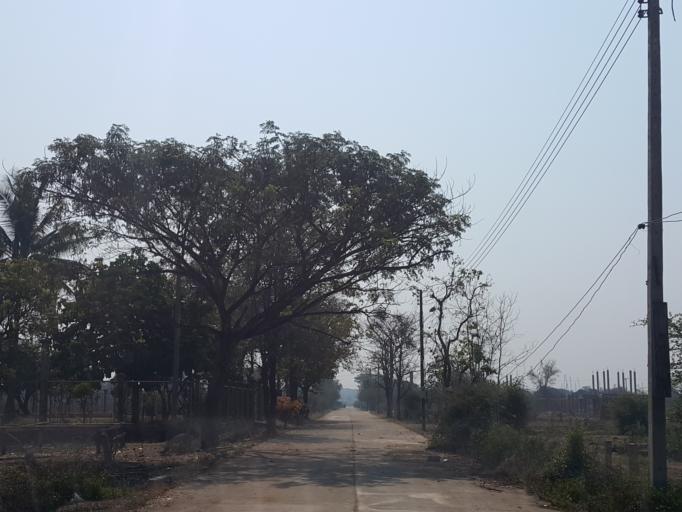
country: TH
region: Chiang Mai
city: San Kamphaeng
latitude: 18.7821
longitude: 99.0723
